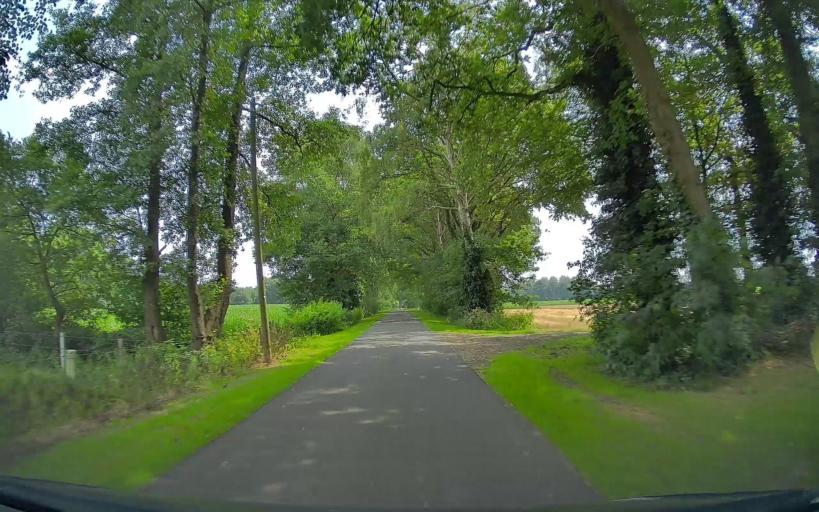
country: DE
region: Lower Saxony
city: Friesoythe
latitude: 52.9918
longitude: 7.8766
